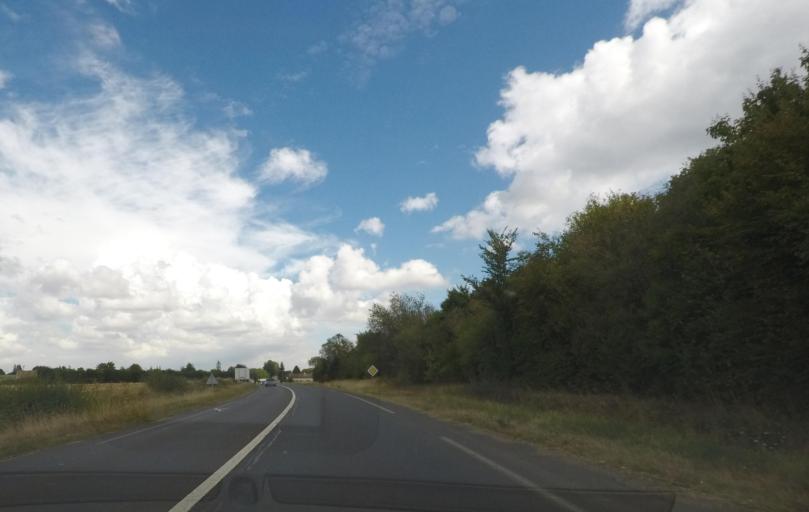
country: FR
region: Pays de la Loire
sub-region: Departement de la Sarthe
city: Champagne
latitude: 48.0820
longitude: 0.3170
